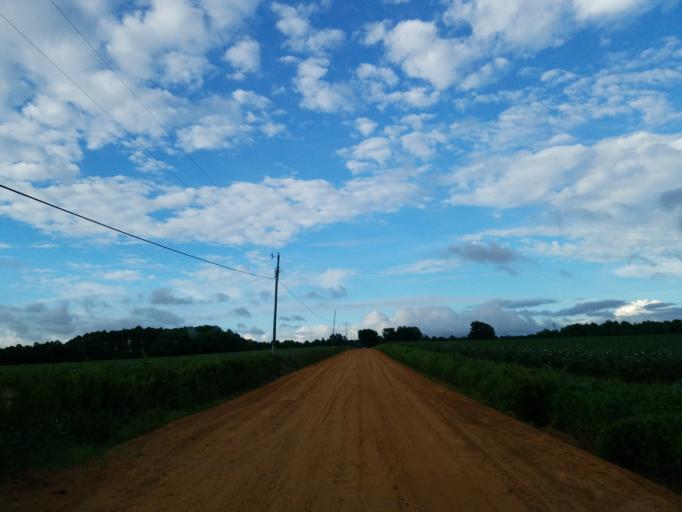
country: US
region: Georgia
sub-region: Cook County
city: Sparks
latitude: 31.2305
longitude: -83.4764
